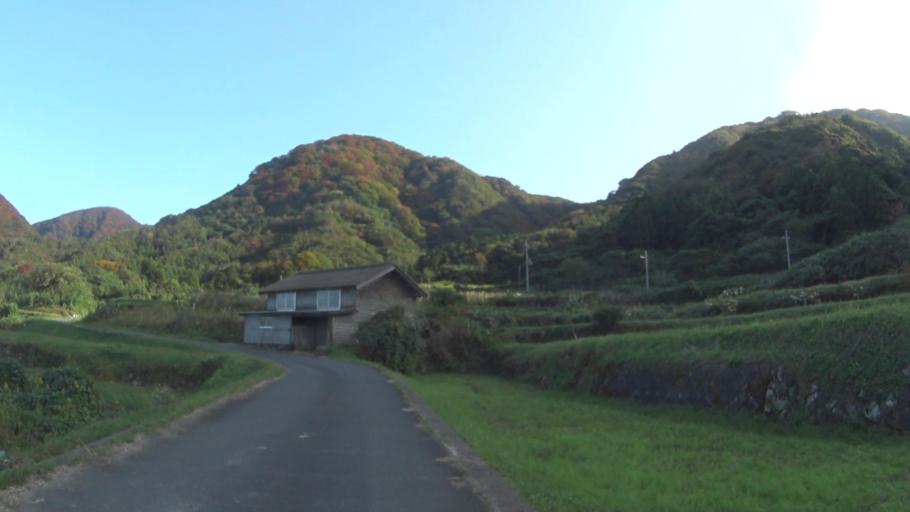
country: JP
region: Kyoto
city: Miyazu
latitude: 35.7615
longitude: 135.2026
